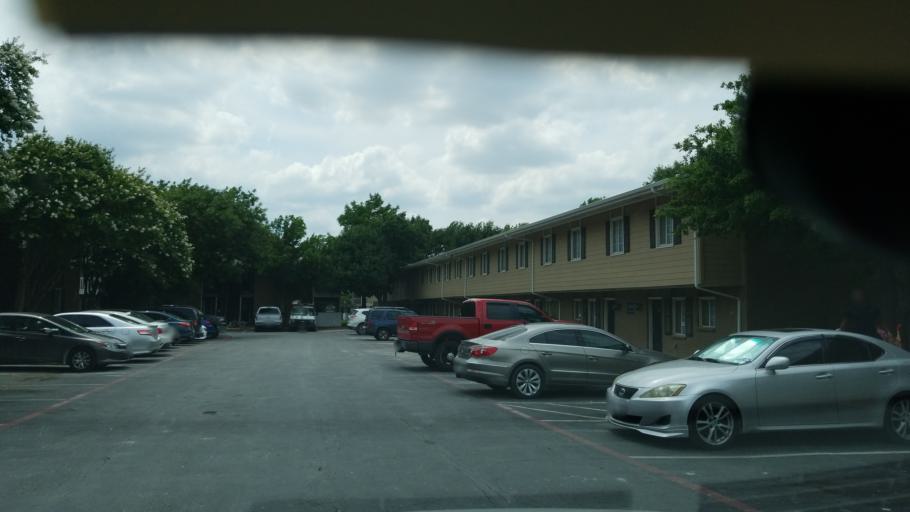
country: US
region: Texas
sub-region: Dallas County
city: Irving
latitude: 32.8408
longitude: -96.9564
